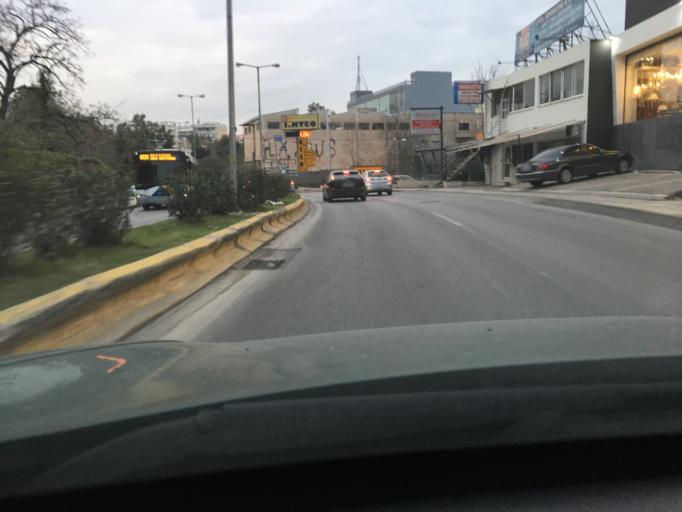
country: GR
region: Attica
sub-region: Nomarchia Athinas
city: Nea Ionia
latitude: 38.0390
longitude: 23.7537
